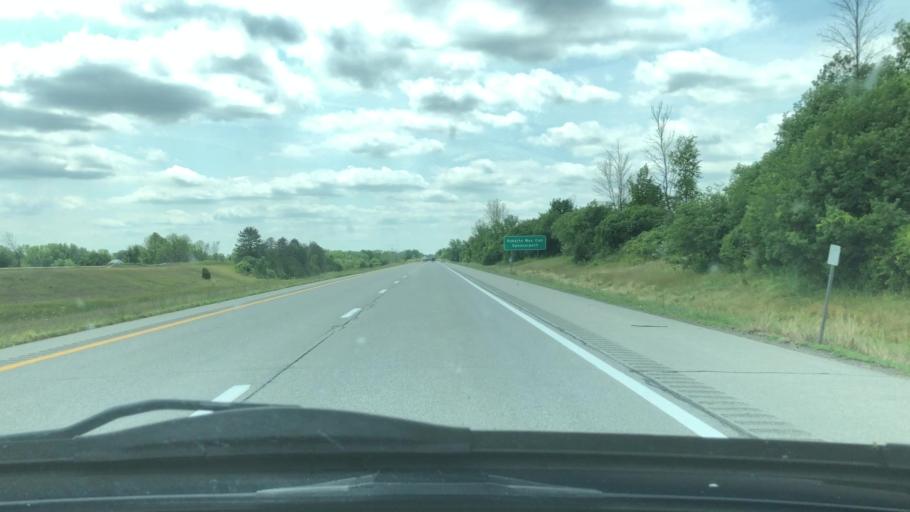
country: US
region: New York
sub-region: Monroe County
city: Spencerport
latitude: 43.1068
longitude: -77.7826
